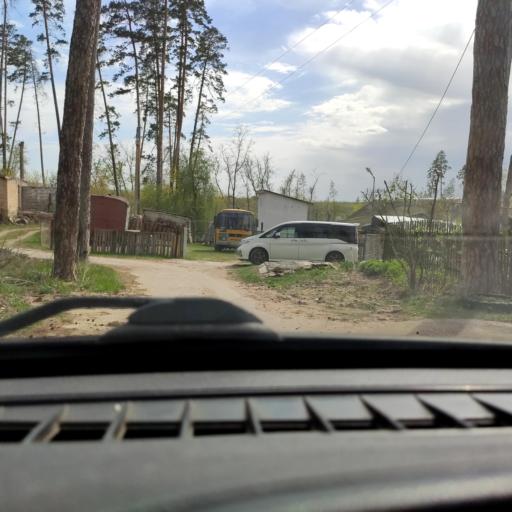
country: RU
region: Samara
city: Tol'yatti
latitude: 53.4998
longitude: 49.3544
